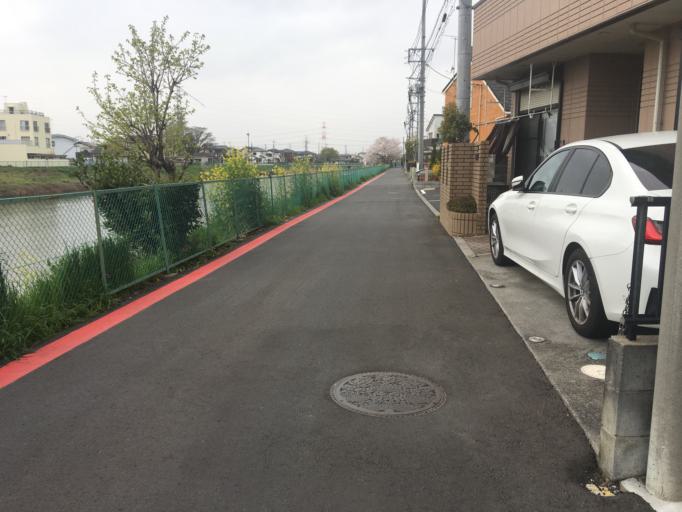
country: JP
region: Saitama
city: Sugito
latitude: 36.0271
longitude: 139.7260
